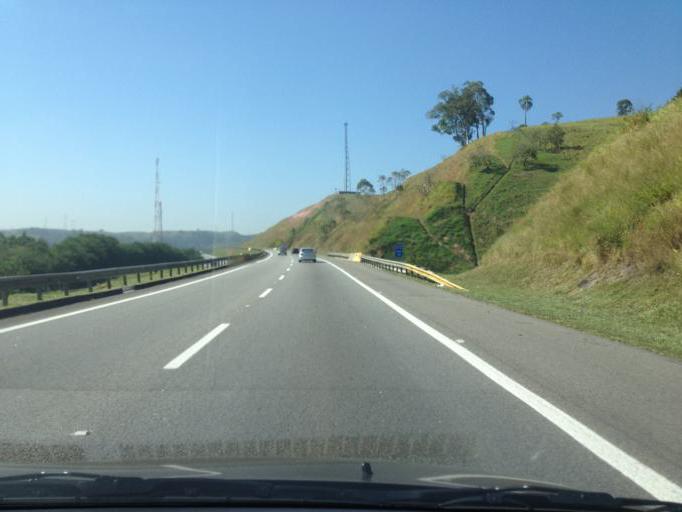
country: BR
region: Sao Paulo
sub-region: Jacarei
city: Jacarei
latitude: -23.3436
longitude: -45.9745
